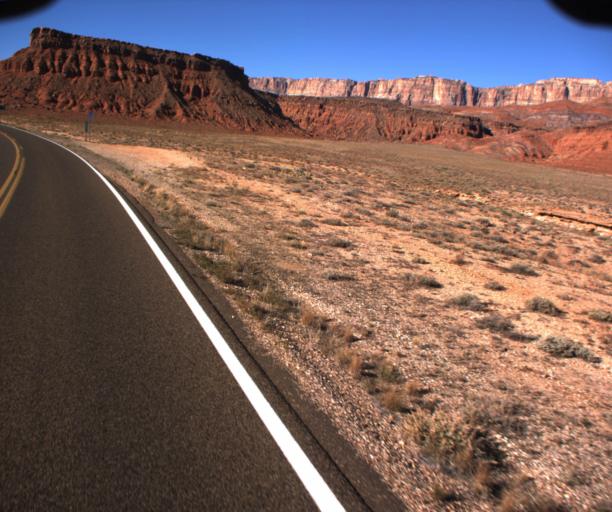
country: US
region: Arizona
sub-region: Coconino County
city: Page
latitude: 36.7651
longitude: -111.7083
